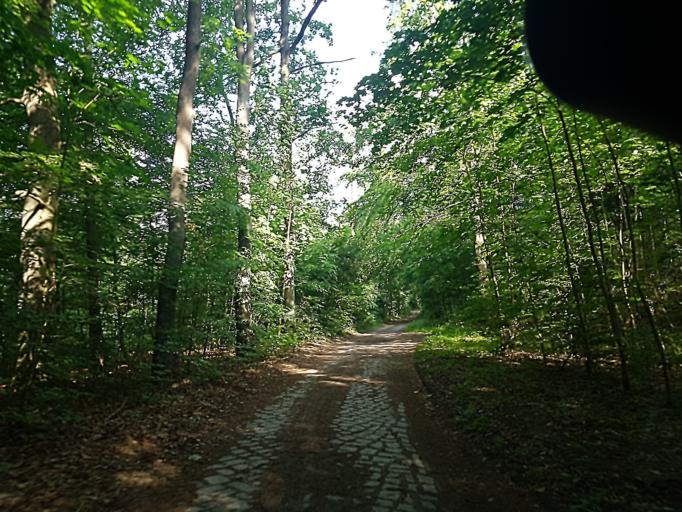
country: DE
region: Brandenburg
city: Wiesenburg
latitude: 52.1000
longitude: 12.4234
